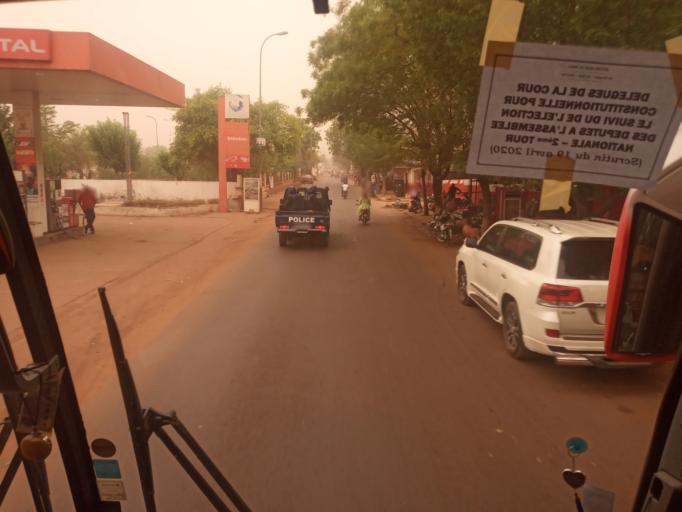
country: ML
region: Bamako
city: Bamako
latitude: 12.6521
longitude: -7.9875
